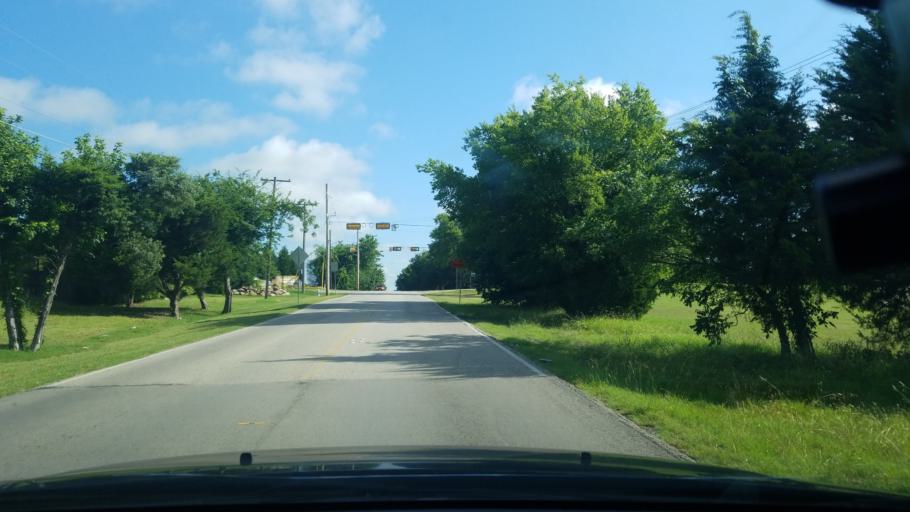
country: US
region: Texas
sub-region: Dallas County
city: Sunnyvale
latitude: 32.8061
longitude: -96.5608
